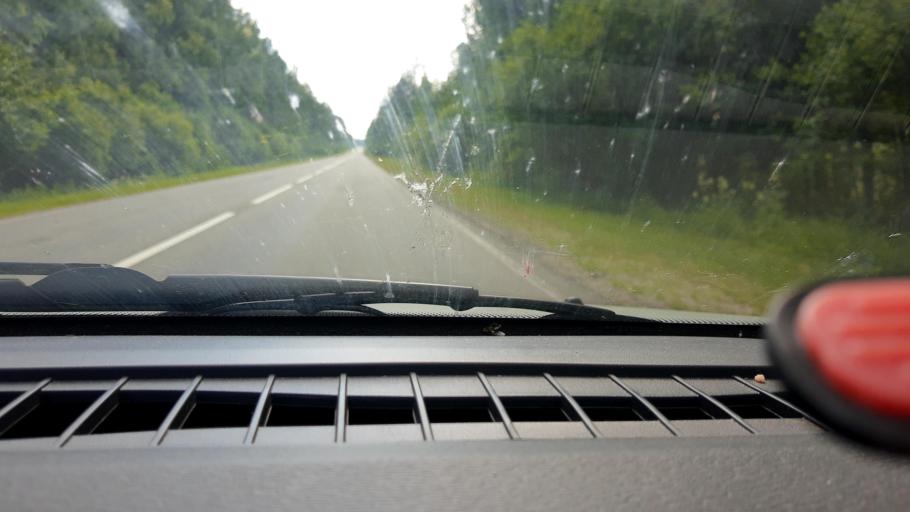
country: RU
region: Nizjnij Novgorod
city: Uren'
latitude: 57.3058
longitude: 45.6734
